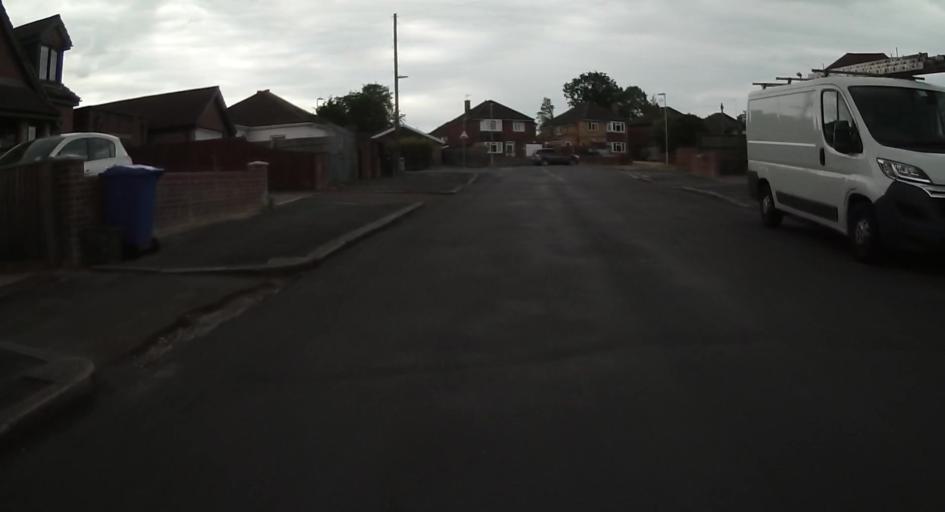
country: GB
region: England
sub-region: Hampshire
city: Aldershot
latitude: 51.2394
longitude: -0.7513
